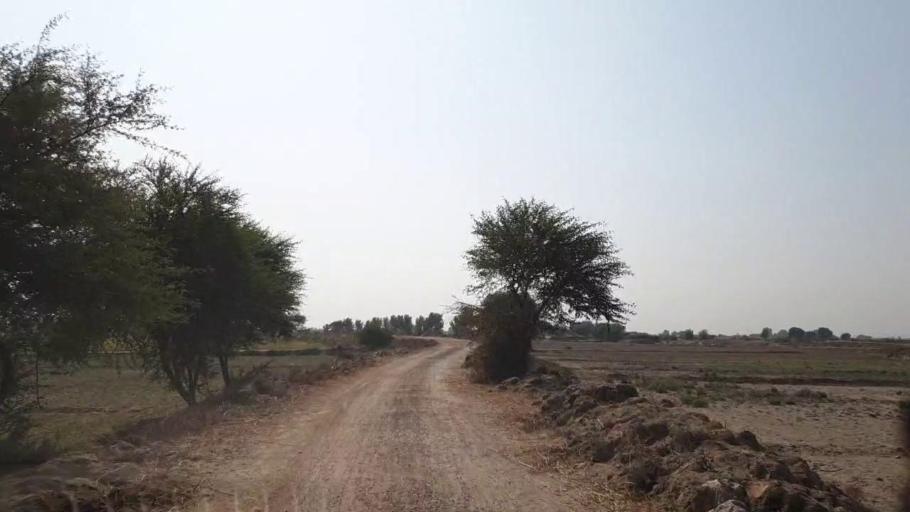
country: PK
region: Sindh
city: Tando Muhammad Khan
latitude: 25.0226
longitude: 68.4170
